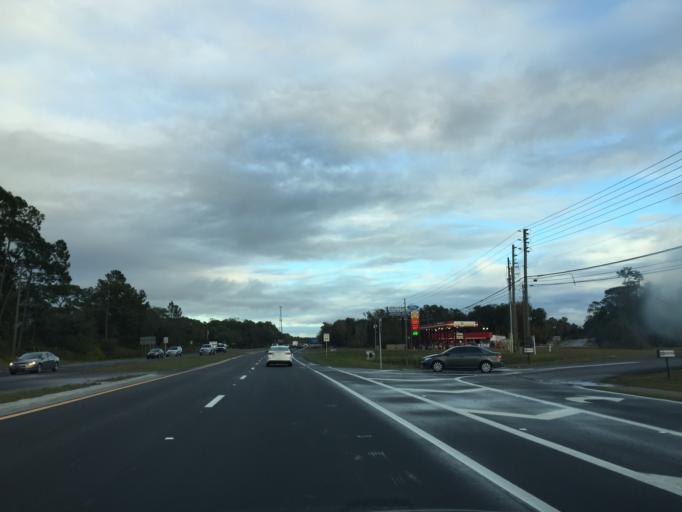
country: US
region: Florida
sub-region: Orange County
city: Alafaya
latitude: 28.5653
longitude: -81.1643
